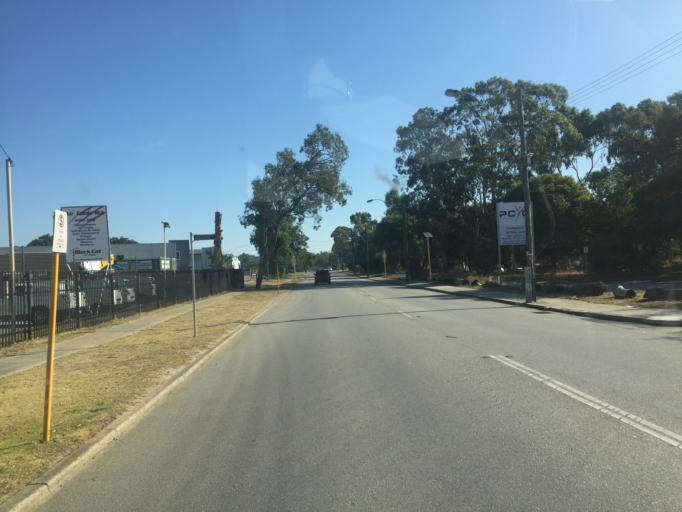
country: AU
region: Western Australia
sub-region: Gosnells
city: Kenwick
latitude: -32.0382
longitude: 115.9680
